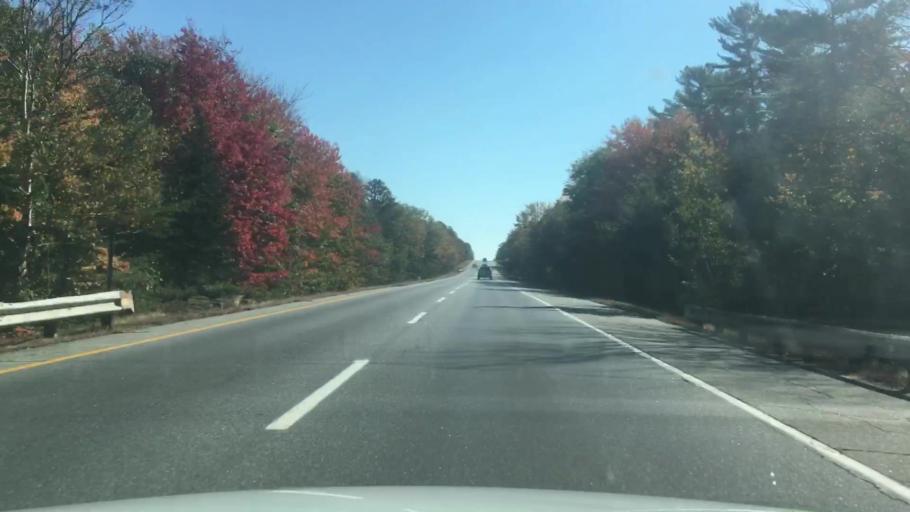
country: US
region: Maine
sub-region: Sagadahoc County
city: Bath
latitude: 43.9129
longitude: -69.8505
